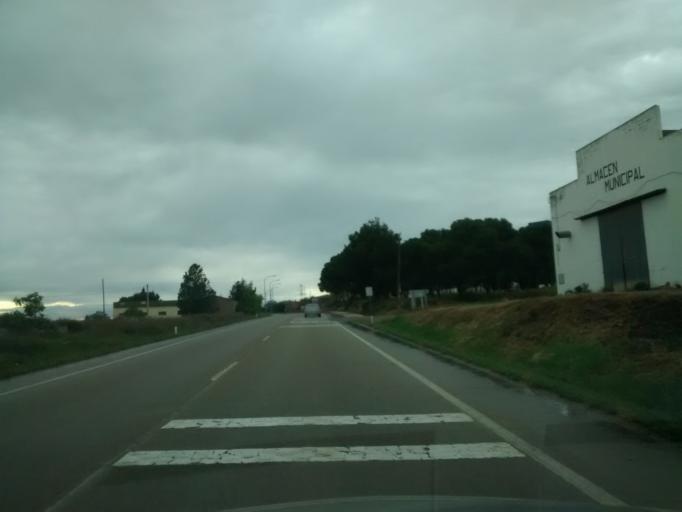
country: ES
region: Aragon
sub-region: Provincia de Zaragoza
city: Caspe
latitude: 41.2248
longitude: -0.0268
